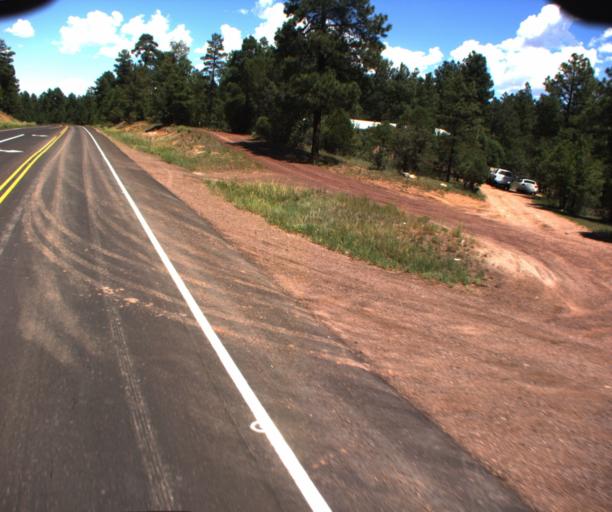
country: US
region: Arizona
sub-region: Navajo County
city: Show Low
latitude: 34.2121
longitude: -110.0752
